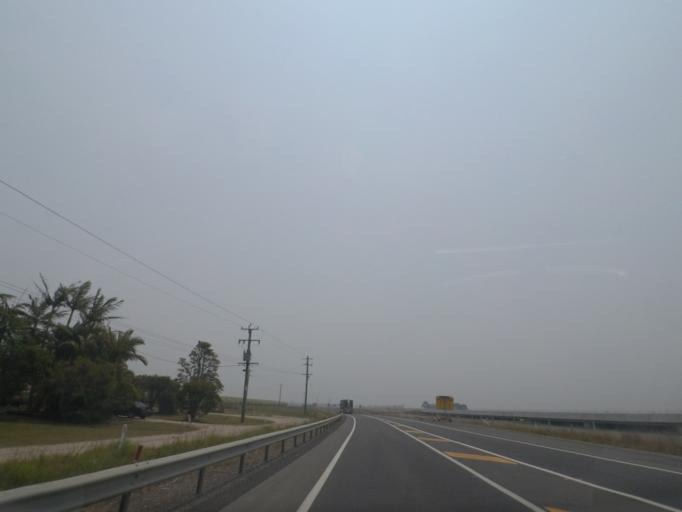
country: AU
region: New South Wales
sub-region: Clarence Valley
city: Maclean
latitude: -29.4175
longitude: 153.2410
